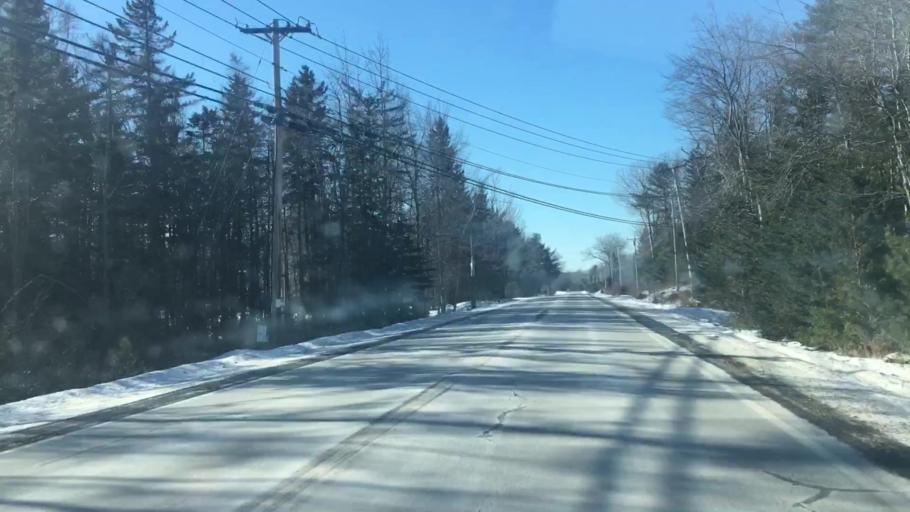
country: US
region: Maine
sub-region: Hancock County
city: Surry
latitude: 44.4943
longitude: -68.4496
